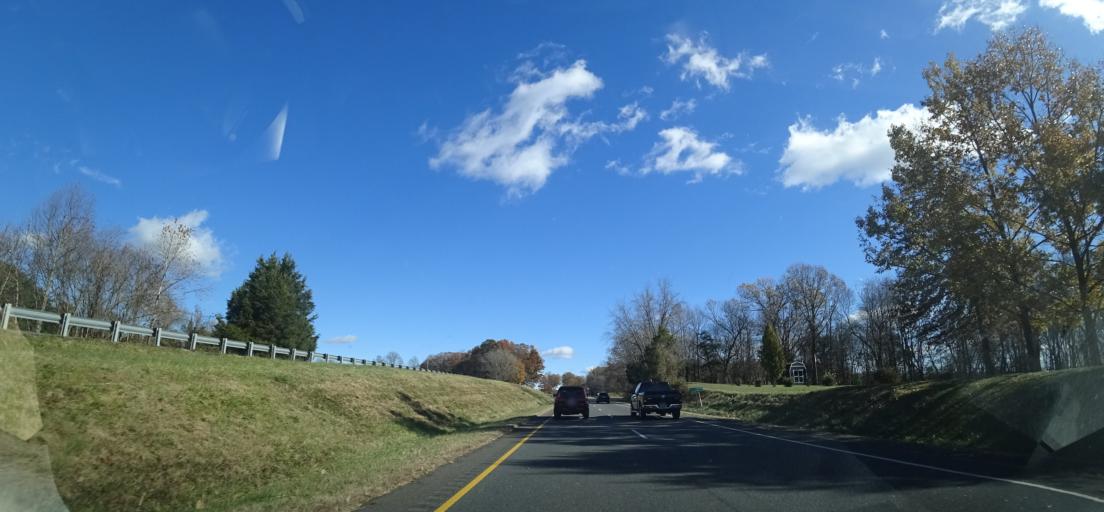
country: US
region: Virginia
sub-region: Madison County
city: Brightwood
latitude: 38.4330
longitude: -78.1601
